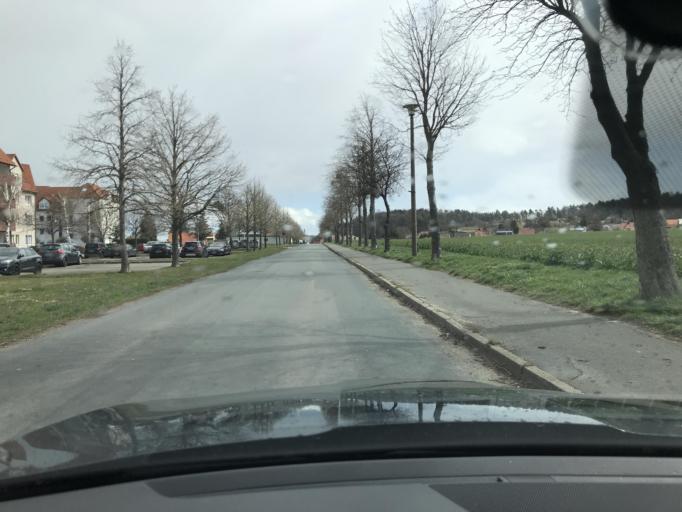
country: DE
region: Saxony-Anhalt
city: Ballenstedt
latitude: 51.7188
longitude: 11.2452
